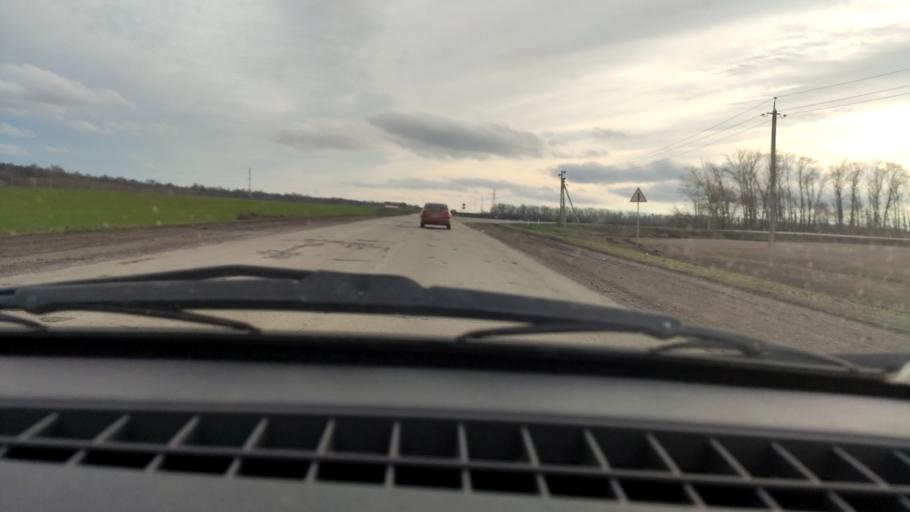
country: RU
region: Bashkortostan
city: Chishmy
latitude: 54.5639
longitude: 55.3467
